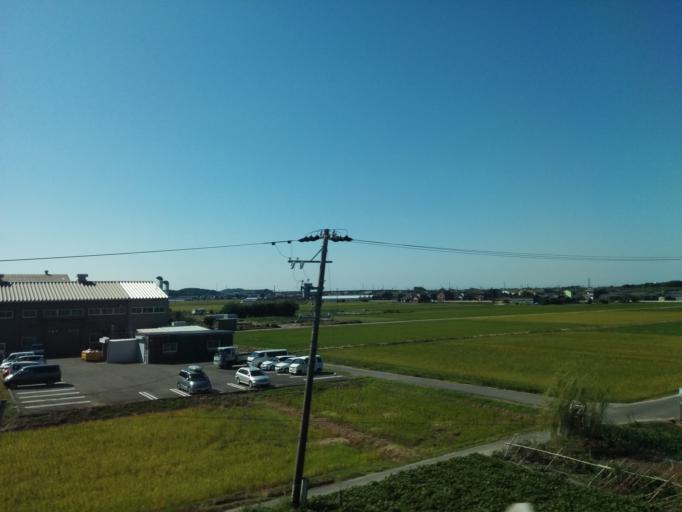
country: JP
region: Aichi
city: Okazaki
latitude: 34.9051
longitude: 137.1193
